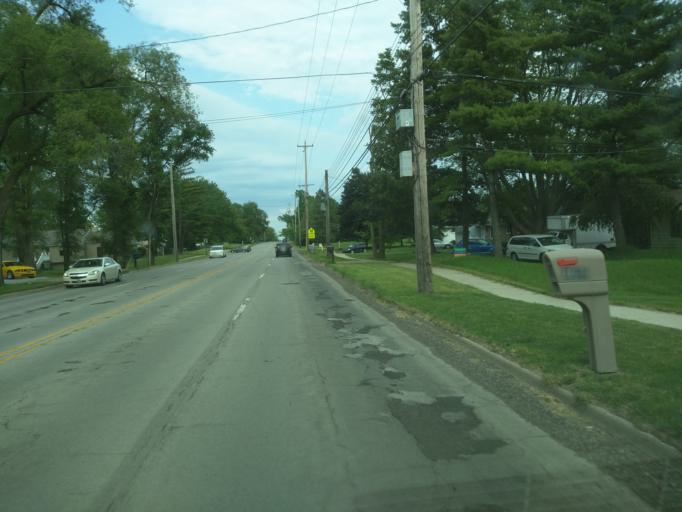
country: US
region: Michigan
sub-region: Eaton County
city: Waverly
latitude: 42.7265
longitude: -84.6155
